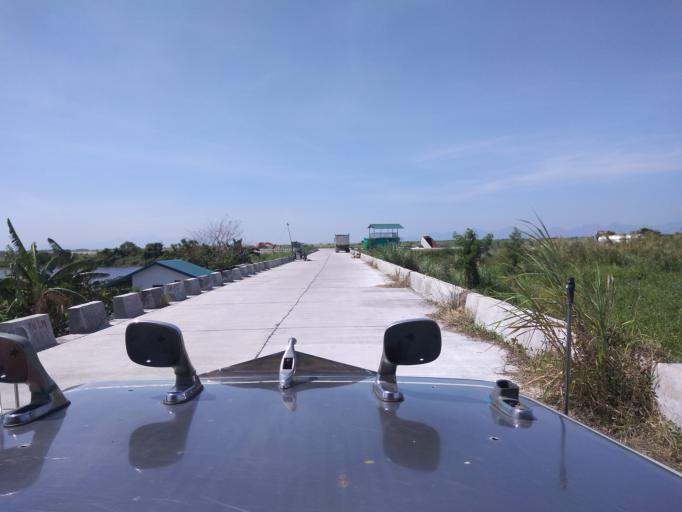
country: PH
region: Central Luzon
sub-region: Province of Pampanga
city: Minalin
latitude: 14.9806
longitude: 120.6848
